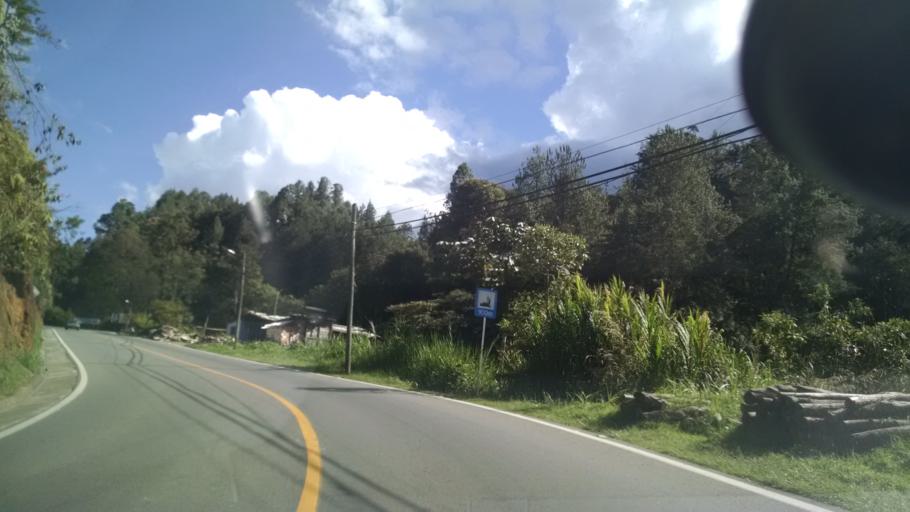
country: CO
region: Antioquia
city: El Retiro
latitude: 6.0840
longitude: -75.4775
